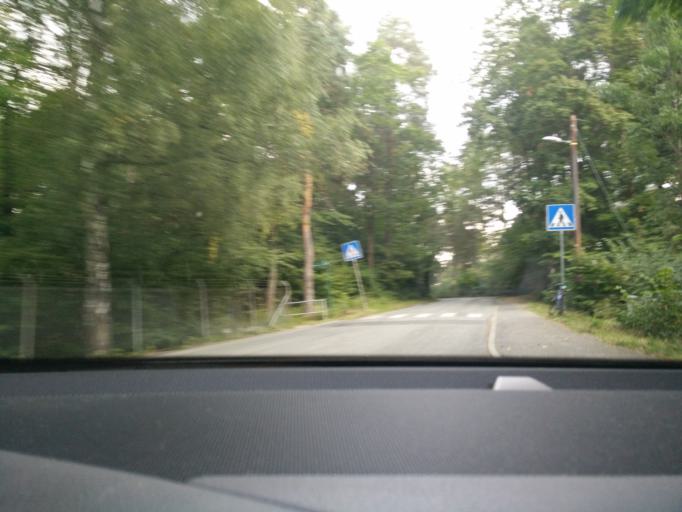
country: NO
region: Oslo
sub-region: Oslo
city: Sjolyststranda
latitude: 59.9063
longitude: 10.6769
